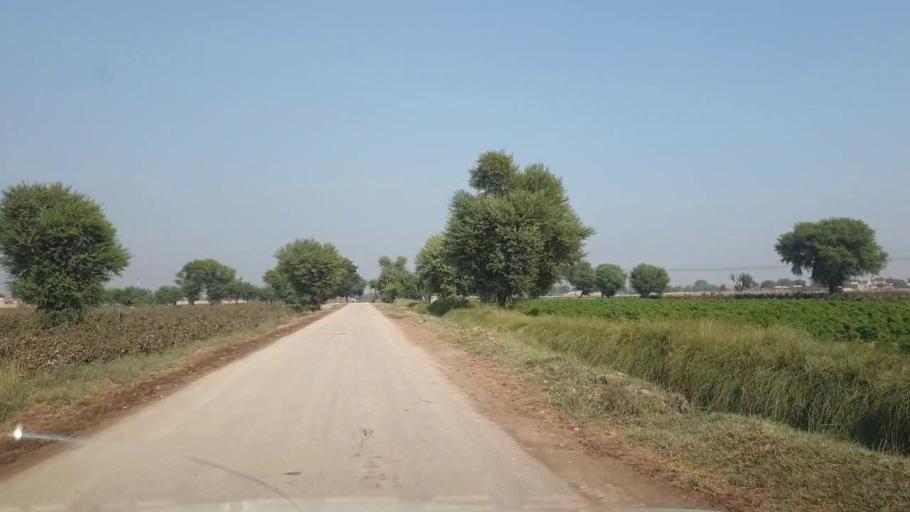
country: PK
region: Sindh
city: Bhan
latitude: 26.5425
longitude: 67.7455
